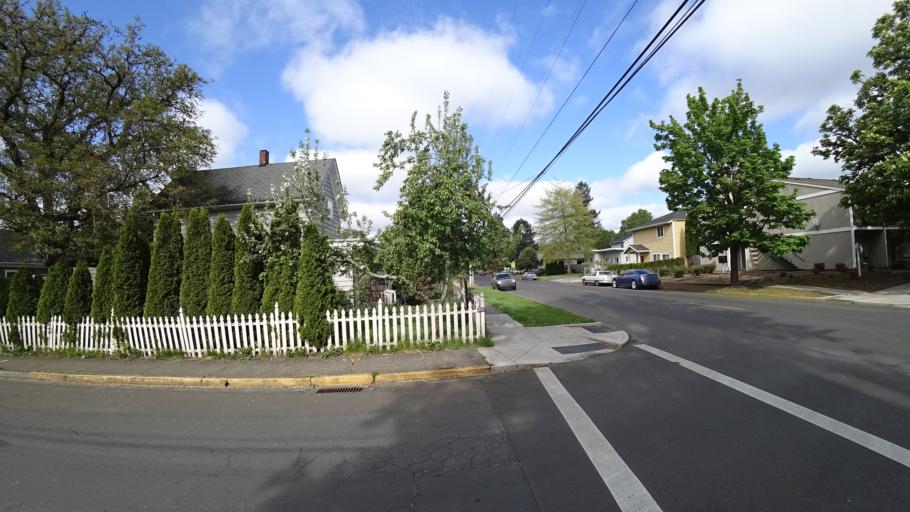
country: US
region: Oregon
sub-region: Washington County
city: Hillsboro
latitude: 45.5174
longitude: -122.9809
